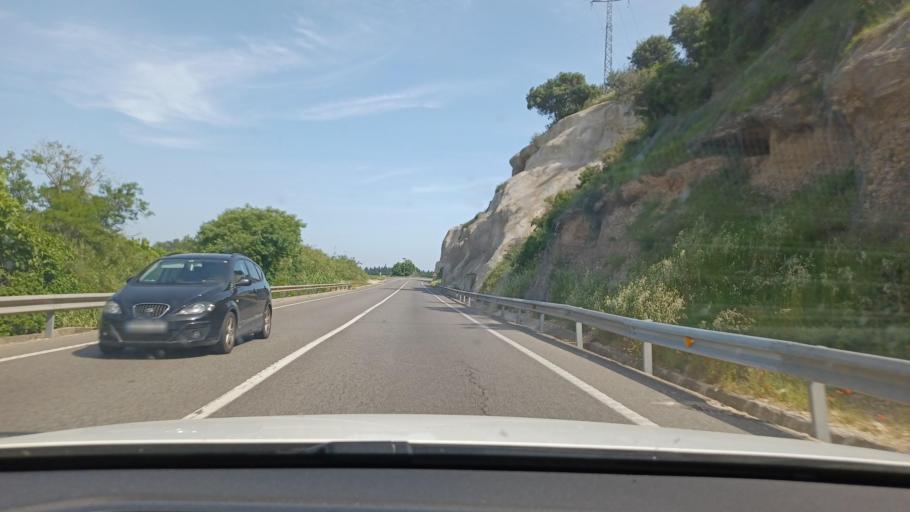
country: ES
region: Catalonia
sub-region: Provincia de Tarragona
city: Tortosa
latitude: 40.7868
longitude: 0.4989
